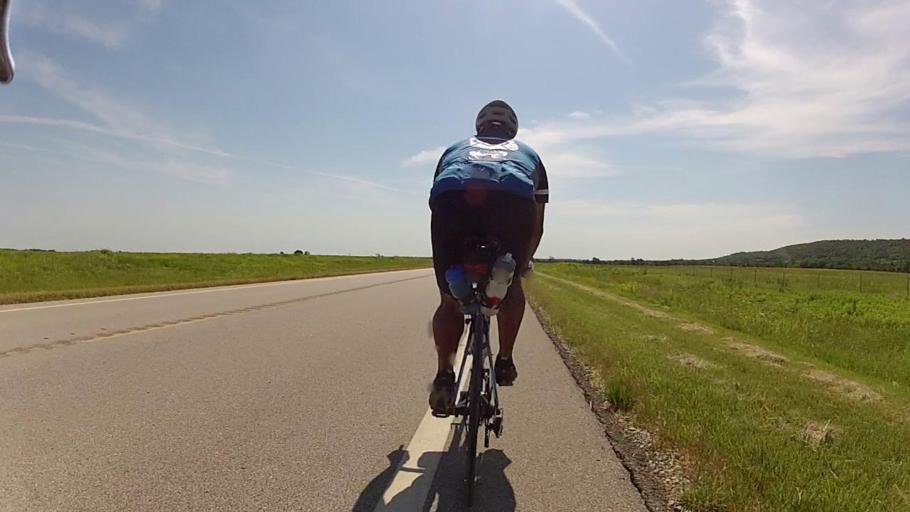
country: US
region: Kansas
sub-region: Chautauqua County
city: Sedan
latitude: 37.1068
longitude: -96.5492
